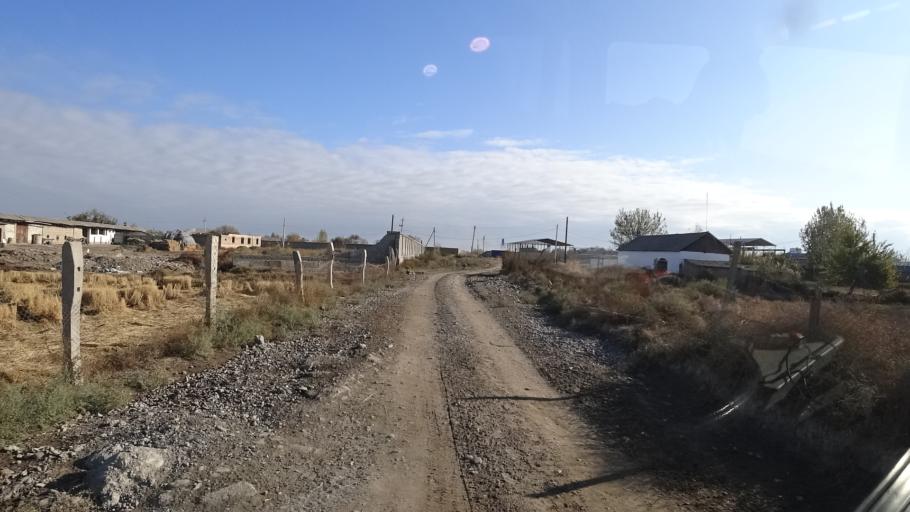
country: UZ
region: Sirdaryo
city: Sirdaryo
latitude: 40.9072
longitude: 68.6800
